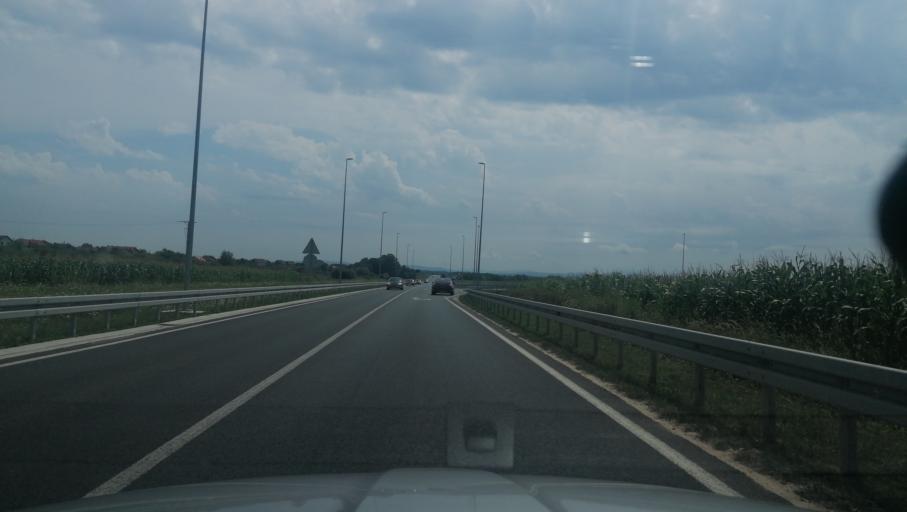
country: BA
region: Brcko
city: Brka
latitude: 44.8587
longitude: 18.7602
